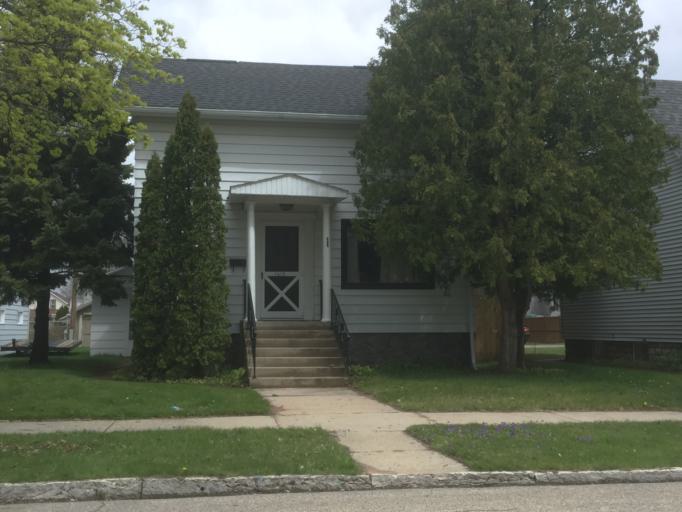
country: US
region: Wisconsin
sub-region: Marinette County
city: Marinette
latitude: 45.0889
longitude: -87.6285
